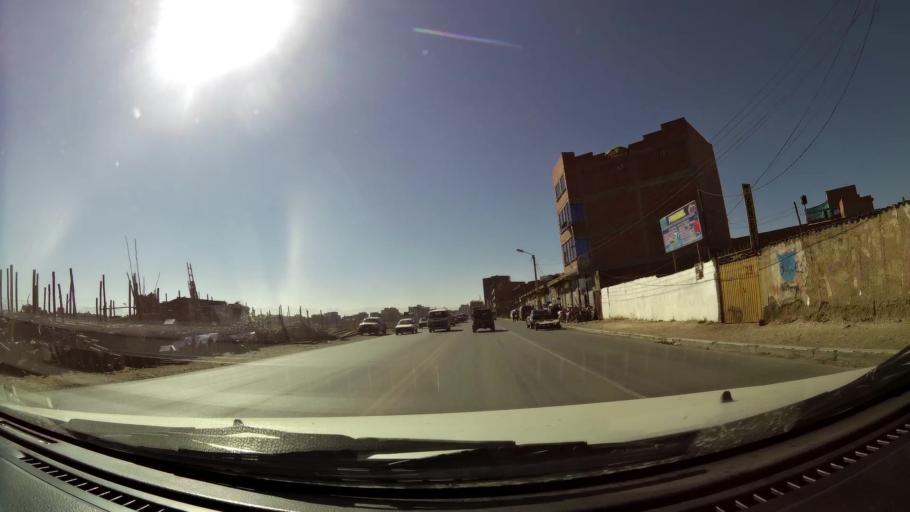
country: BO
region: La Paz
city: La Paz
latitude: -16.5165
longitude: -68.1719
